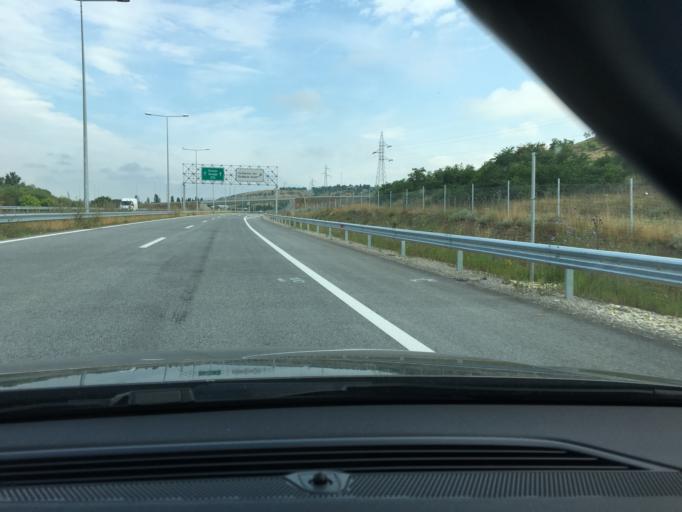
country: MK
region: Sveti Nikole
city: Sveti Nikole
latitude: 41.8536
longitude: 21.9640
